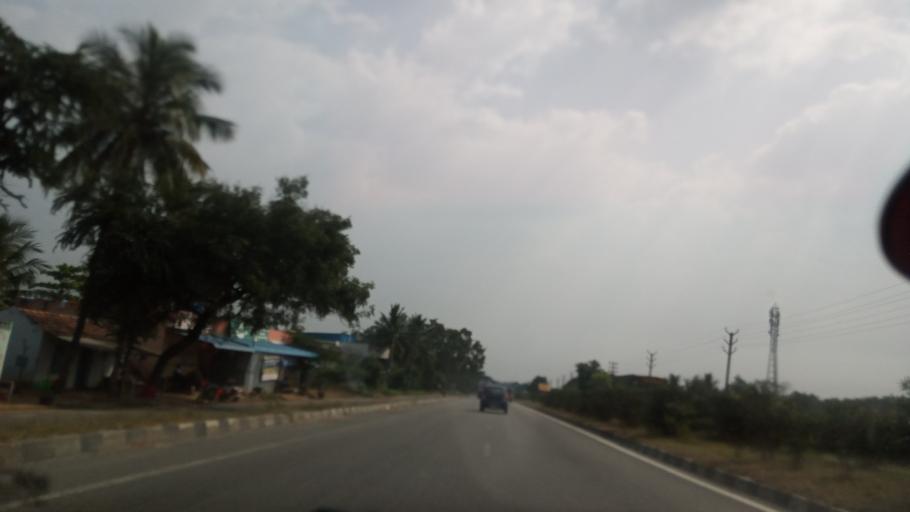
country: IN
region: Tamil Nadu
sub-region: Salem
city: Omalur
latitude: 11.7928
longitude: 78.0570
